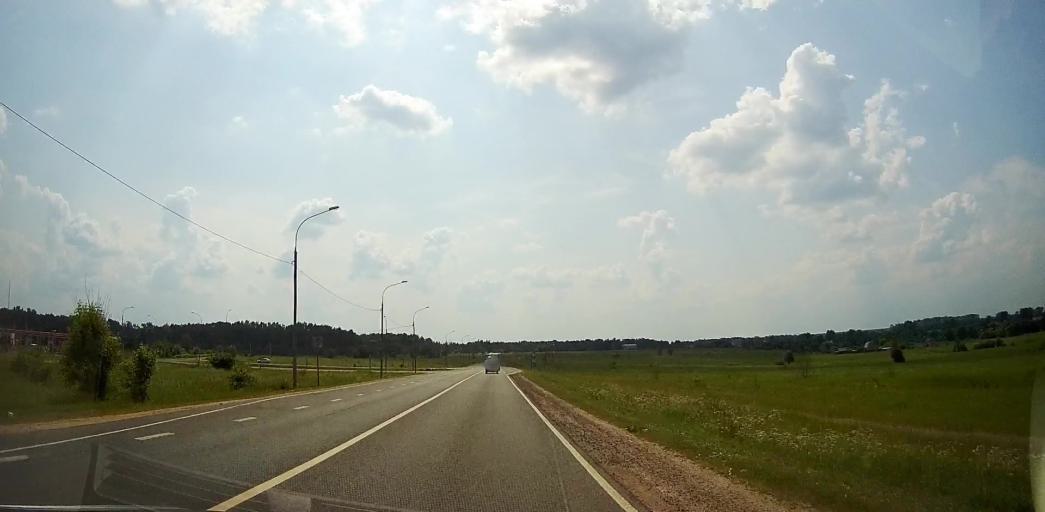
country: RU
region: Moskovskaya
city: Malino
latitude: 55.1011
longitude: 38.1701
